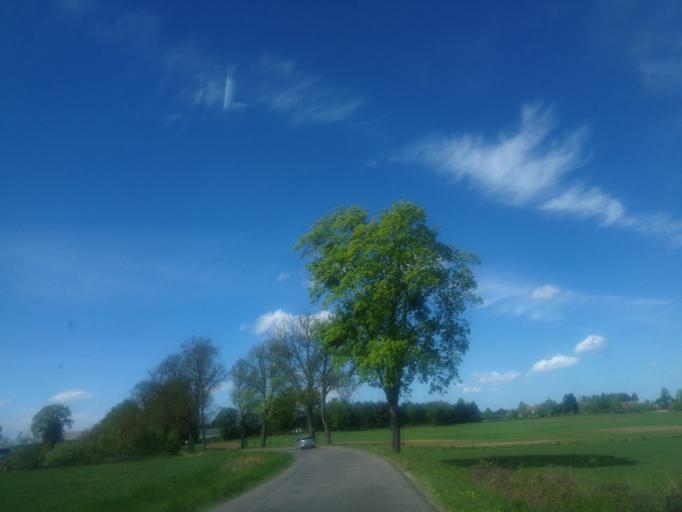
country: PL
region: Warmian-Masurian Voivodeship
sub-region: Powiat ilawski
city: Zalewo
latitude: 53.7585
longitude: 19.6888
